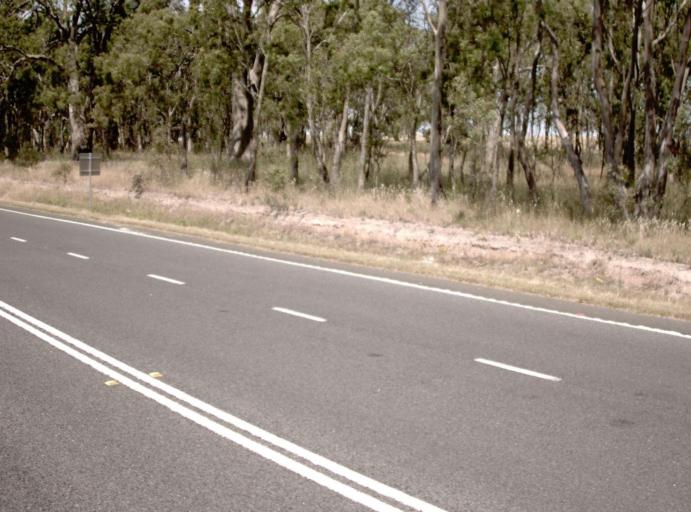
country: AU
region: Victoria
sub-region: Latrobe
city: Traralgon
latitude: -38.1727
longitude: 146.6659
